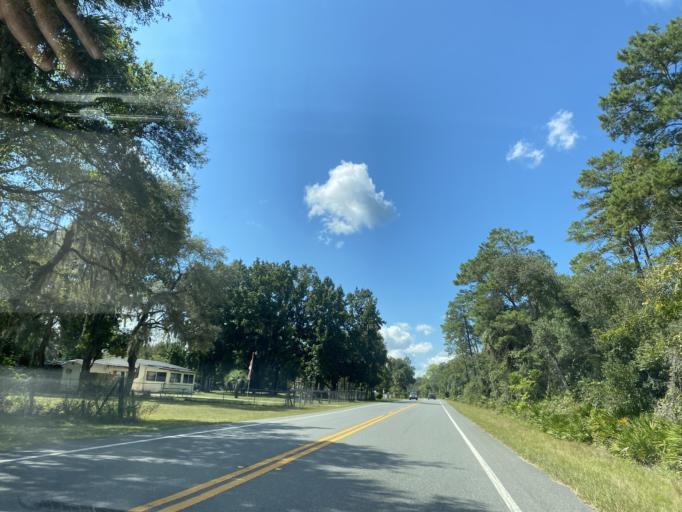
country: US
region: Florida
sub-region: Lake County
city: Lake Mack-Forest Hills
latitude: 29.0173
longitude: -81.4791
